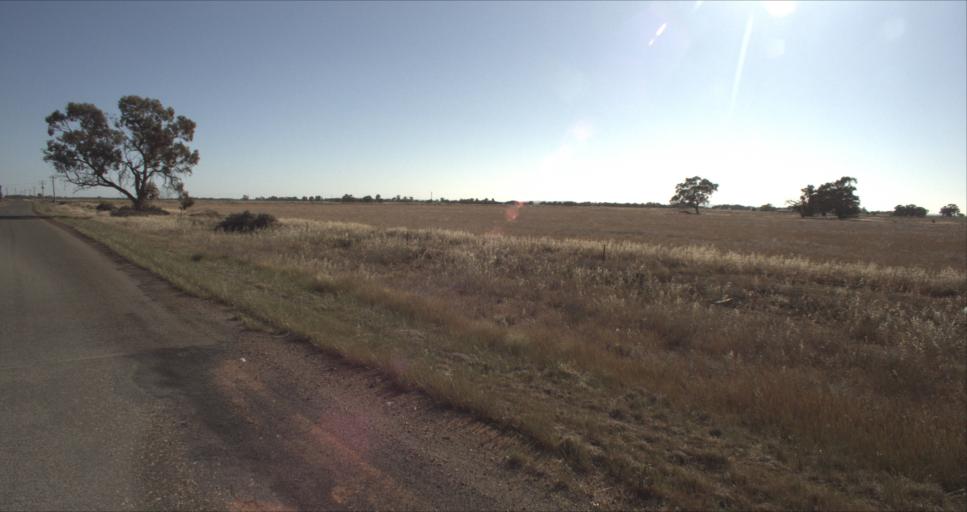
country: AU
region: New South Wales
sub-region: Leeton
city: Leeton
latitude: -34.5573
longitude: 146.2661
